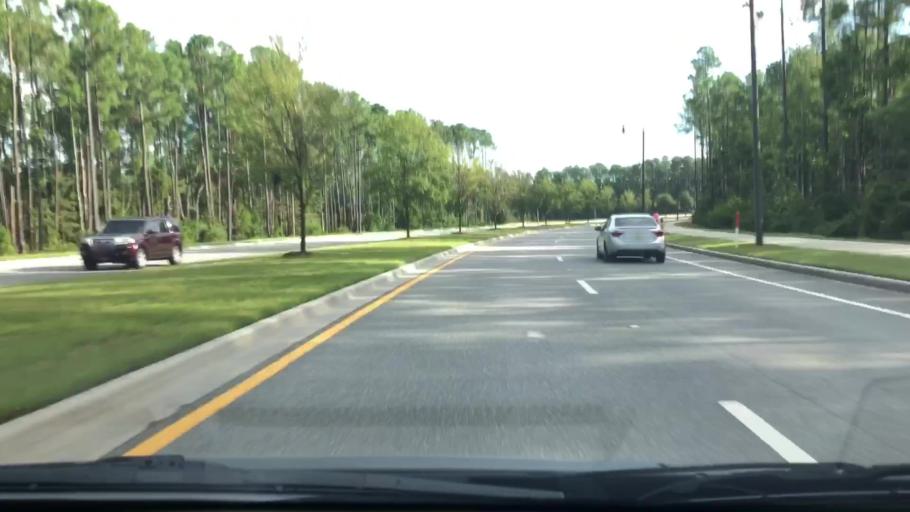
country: US
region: Florida
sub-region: Saint Johns County
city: Palm Valley
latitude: 30.1184
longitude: -81.4497
